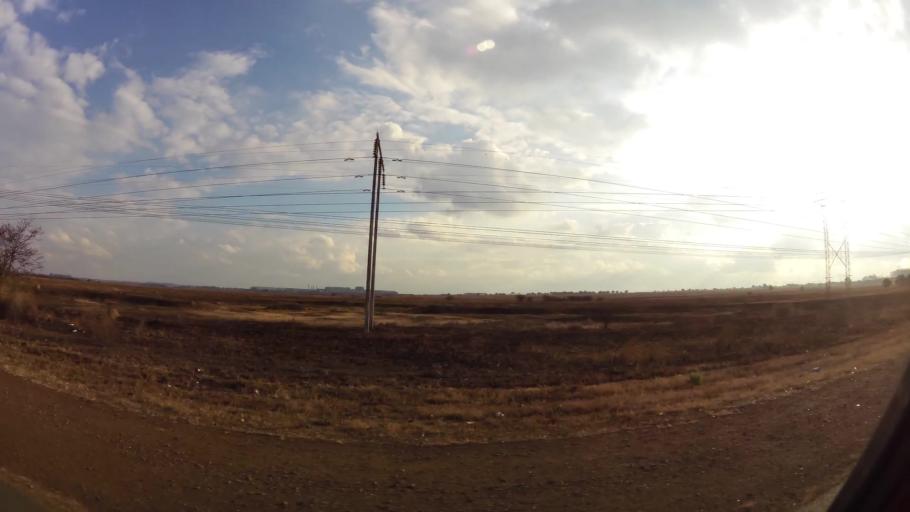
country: ZA
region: Gauteng
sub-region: Sedibeng District Municipality
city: Vereeniging
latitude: -26.6292
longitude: 27.8667
